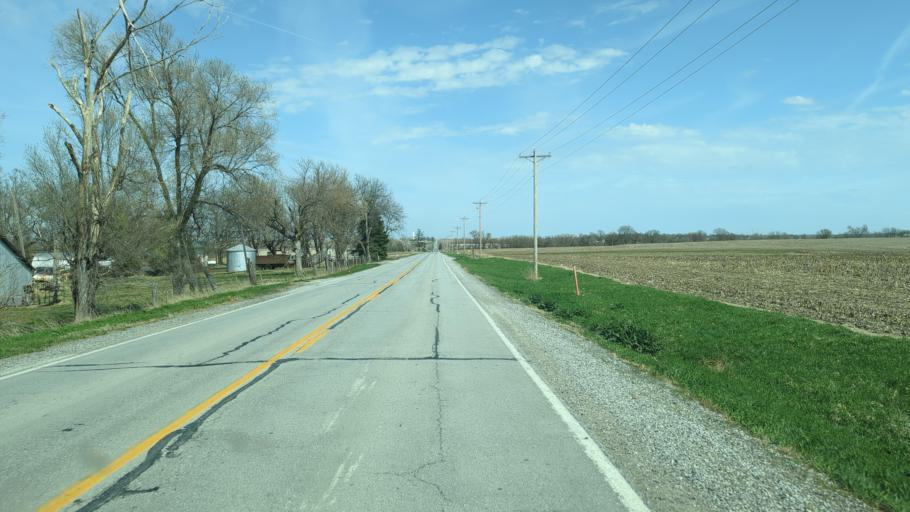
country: US
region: Nebraska
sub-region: Sarpy County
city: Springfield
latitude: 41.0889
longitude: -96.1548
